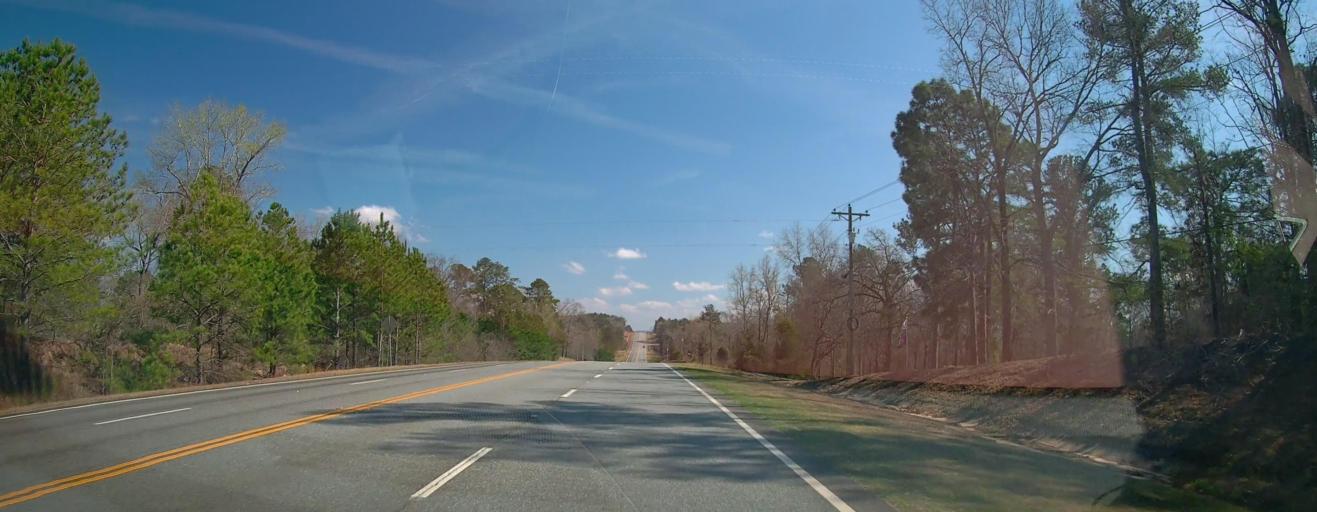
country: US
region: Georgia
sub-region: Wilkinson County
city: Gordon
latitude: 32.9178
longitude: -83.3903
